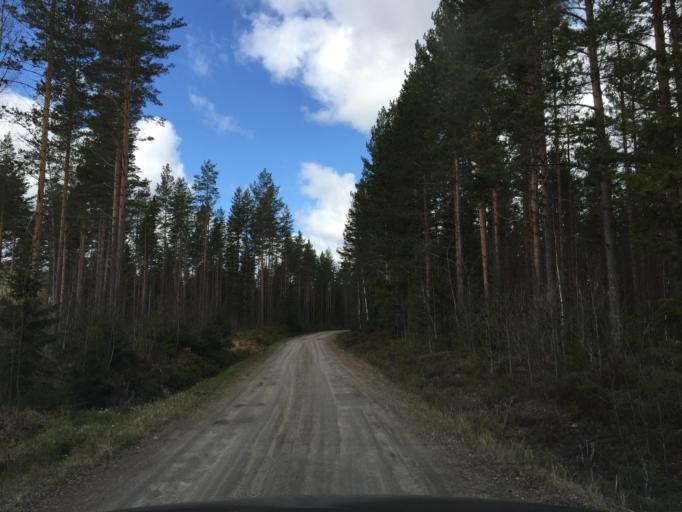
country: SE
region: Gaevleborg
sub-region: Bollnas Kommun
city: Arbra
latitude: 61.5227
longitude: 16.2890
